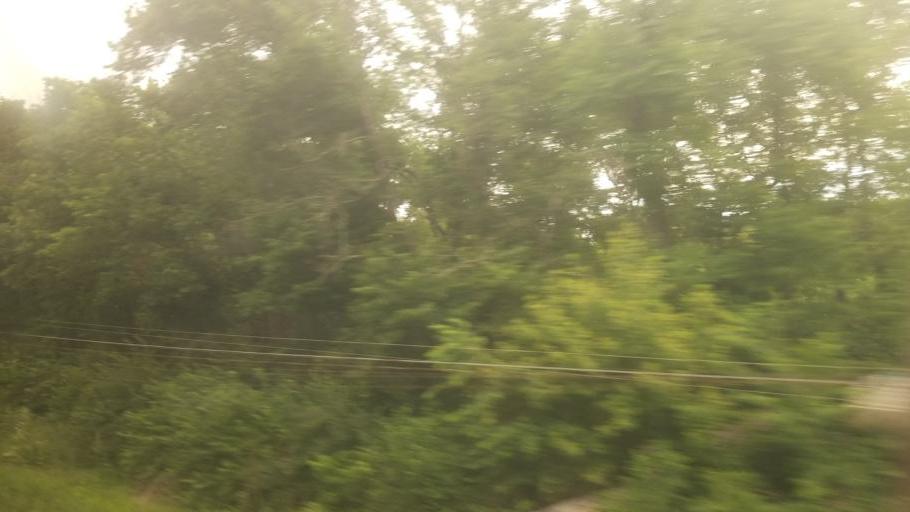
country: US
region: Kansas
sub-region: Osage County
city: Carbondale
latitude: 38.8909
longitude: -95.6970
